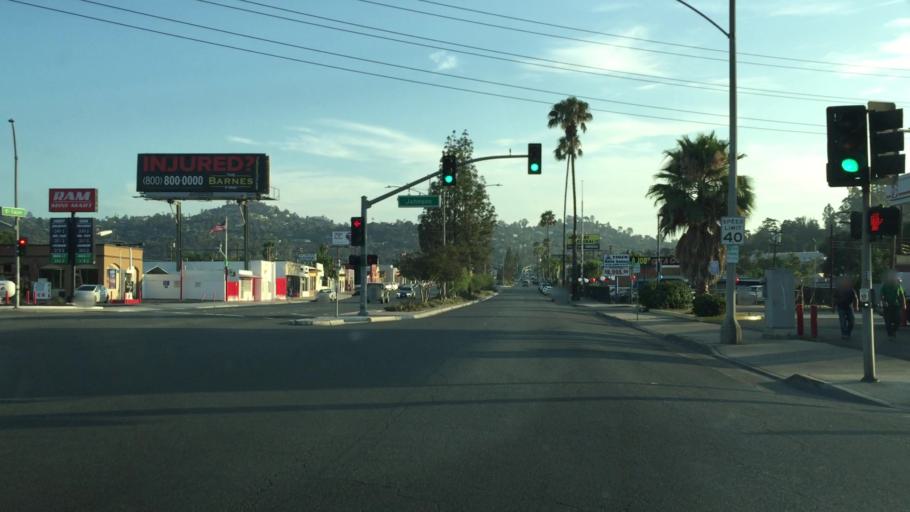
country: US
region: California
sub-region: San Diego County
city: El Cajon
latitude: 32.7917
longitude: -116.9711
